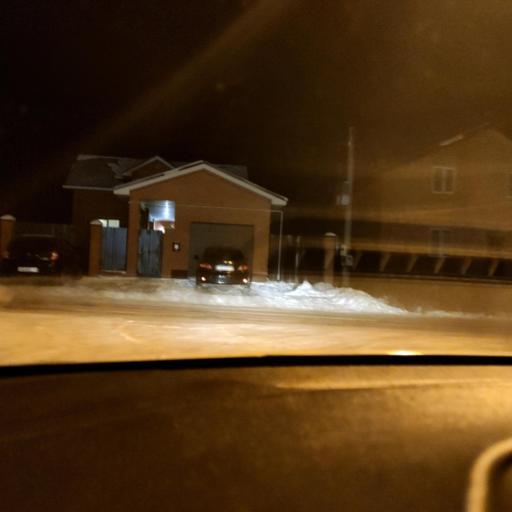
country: RU
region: Tatarstan
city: Stolbishchi
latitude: 55.7529
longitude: 49.2715
